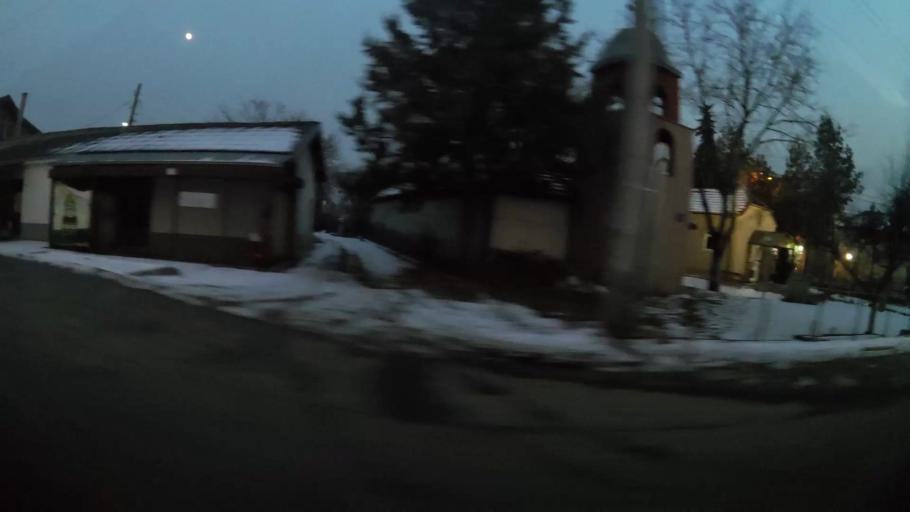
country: MK
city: Creshevo
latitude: 42.0041
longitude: 21.5167
